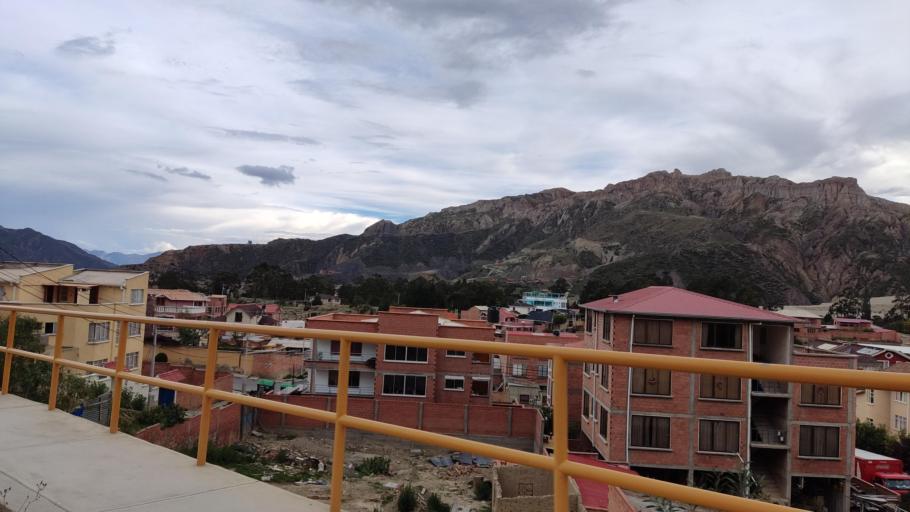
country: BO
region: La Paz
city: La Paz
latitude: -16.5649
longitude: -68.0981
